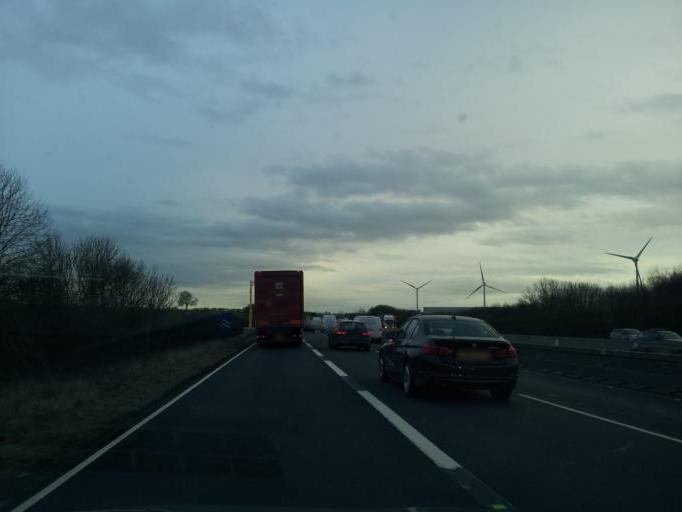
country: GB
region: England
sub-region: Northamptonshire
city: Long Buckby
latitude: 52.3588
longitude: -1.1562
